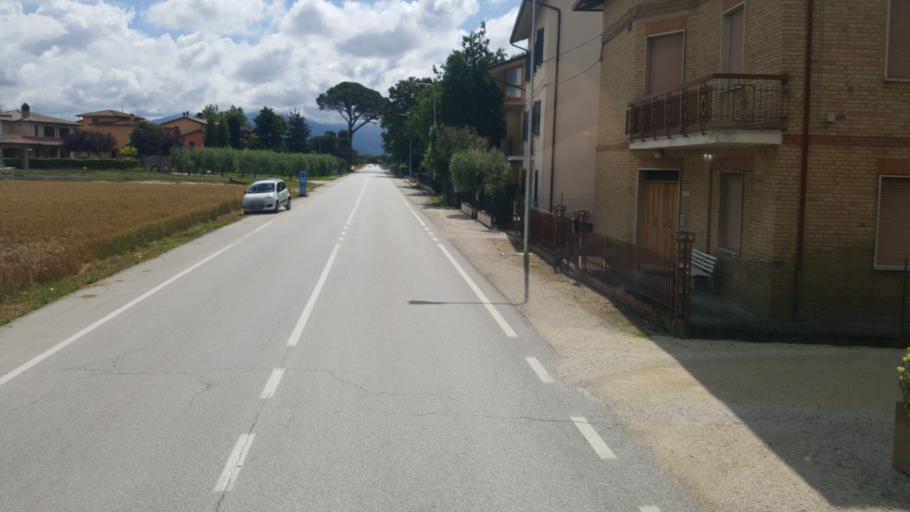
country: IT
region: Umbria
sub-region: Provincia di Perugia
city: Ospedalicchio
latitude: 43.0644
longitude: 12.5144
